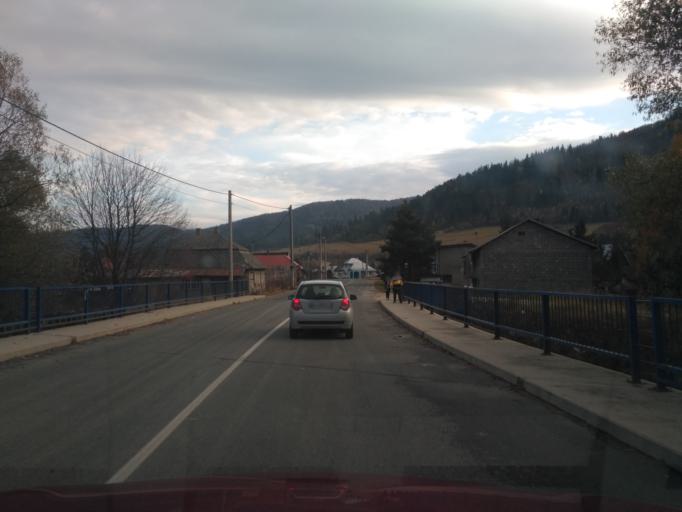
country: SK
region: Kosicky
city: Krompachy
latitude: 48.8088
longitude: 20.7239
